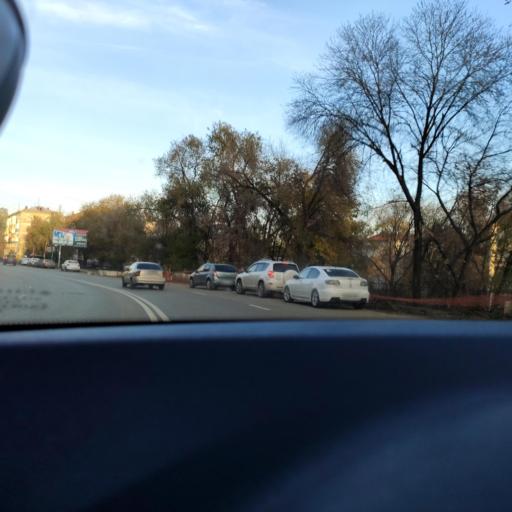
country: RU
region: Samara
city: Samara
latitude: 53.2068
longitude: 50.2258
